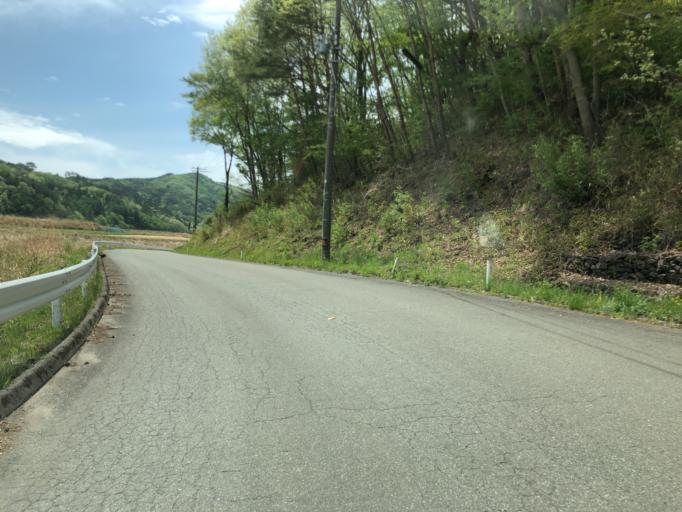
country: JP
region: Fukushima
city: Yanagawamachi-saiwaicho
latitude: 37.7213
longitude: 140.7241
